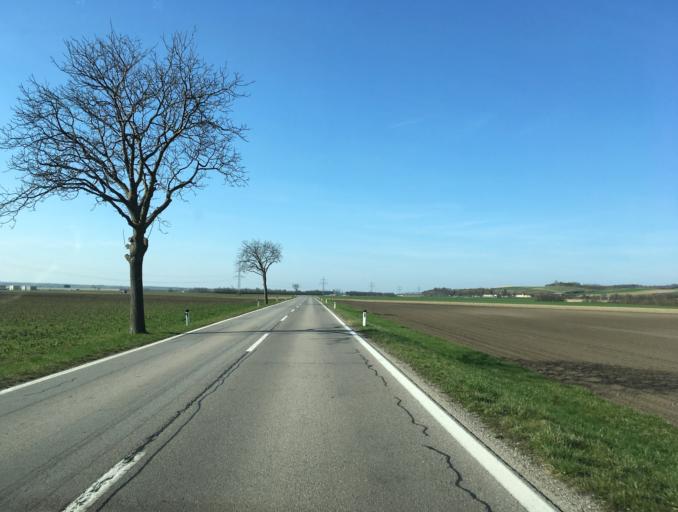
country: AT
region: Lower Austria
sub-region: Politischer Bezirk Bruck an der Leitha
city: Trautmannsdorf an der Leitha
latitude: 48.0487
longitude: 16.6199
